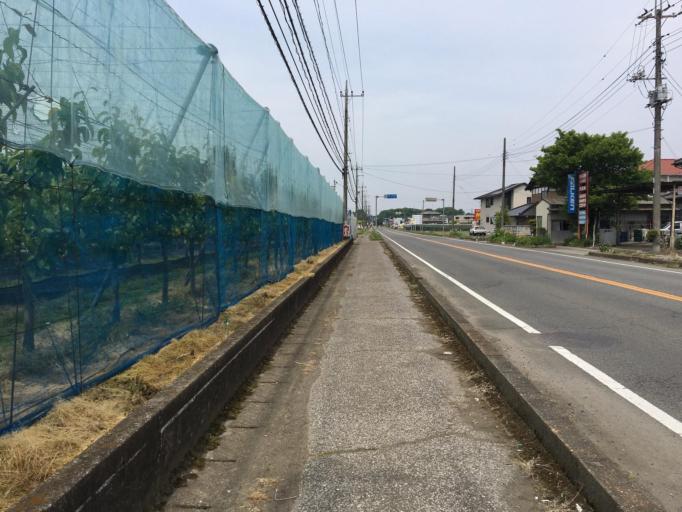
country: JP
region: Tochigi
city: Oyama
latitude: 36.3489
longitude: 139.8133
